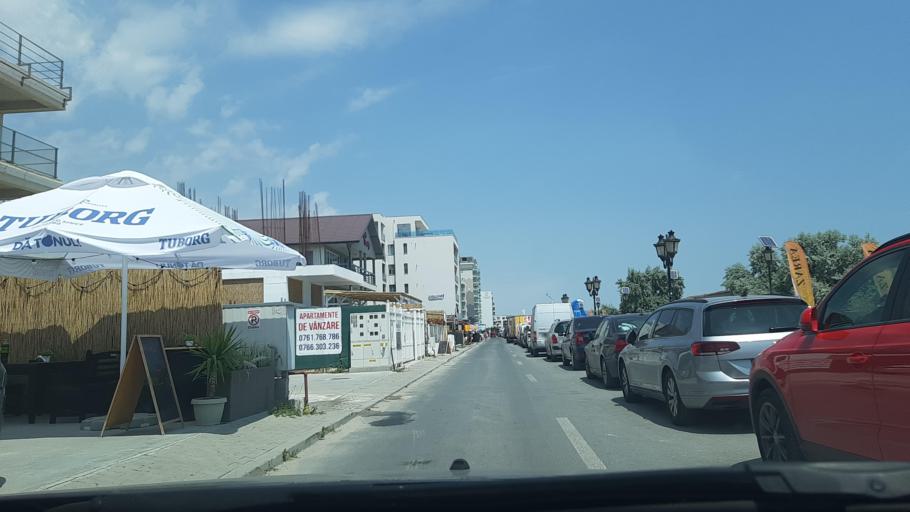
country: RO
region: Constanta
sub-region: Comuna Navodari
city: Navodari
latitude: 44.2908
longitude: 28.6234
